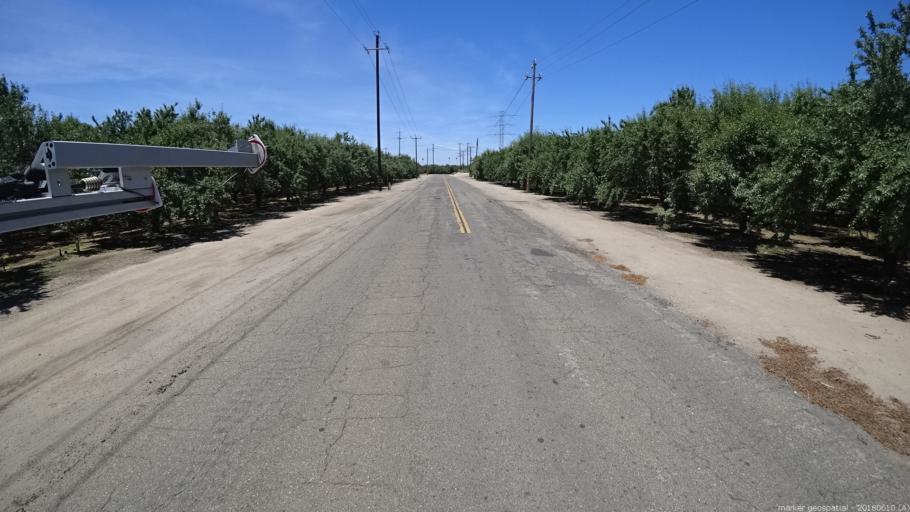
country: US
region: California
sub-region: Madera County
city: Chowchilla
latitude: 37.0544
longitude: -120.3148
